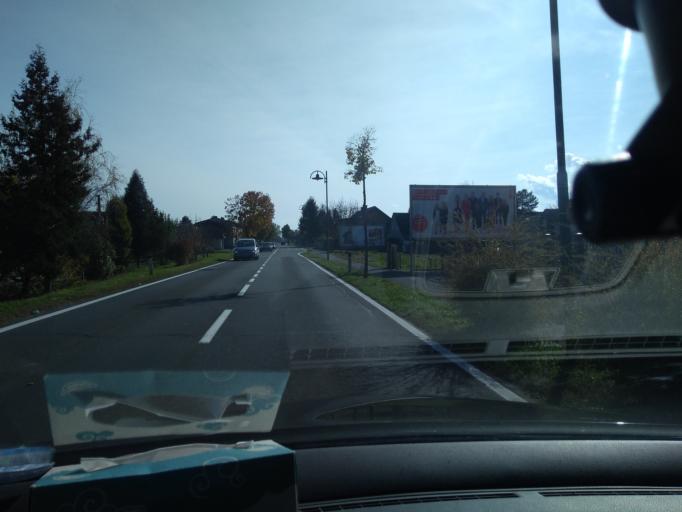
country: AT
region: Styria
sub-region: Politischer Bezirk Leibnitz
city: Kaindorf an der Sulm
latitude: 46.8220
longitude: 15.5457
